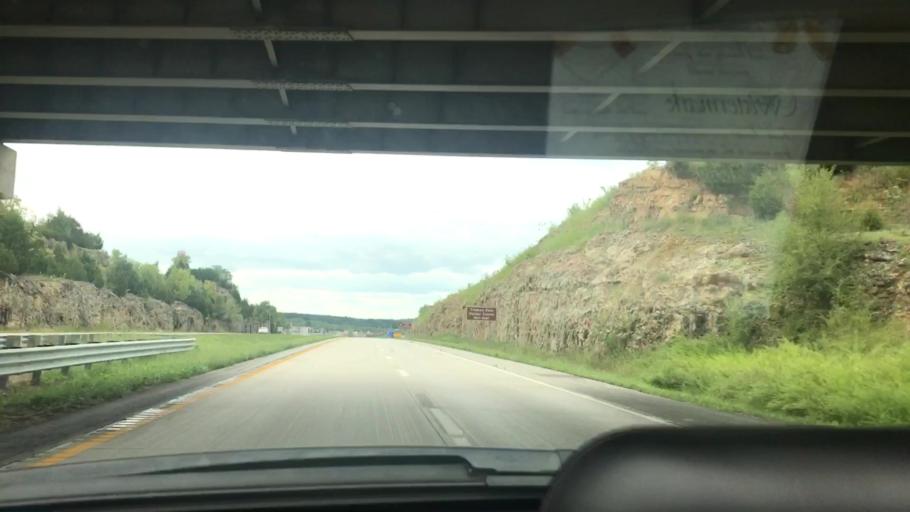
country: US
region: Missouri
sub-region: Benton County
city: Warsaw
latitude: 38.2535
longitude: -93.3641
